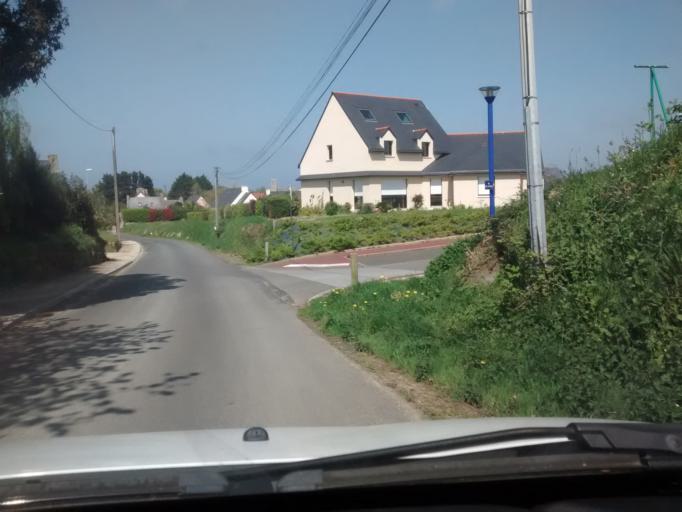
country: FR
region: Brittany
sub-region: Departement des Cotes-d'Armor
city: Louannec
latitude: 48.7890
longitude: -3.4118
